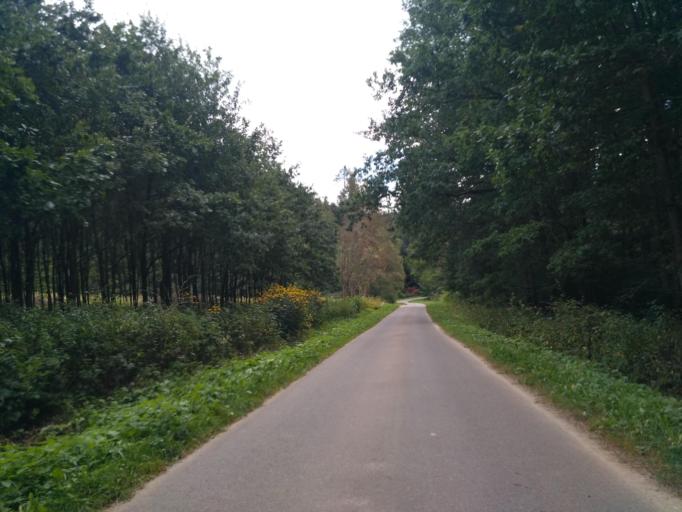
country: PL
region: Subcarpathian Voivodeship
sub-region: Powiat rzeszowski
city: Dynow
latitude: 49.7576
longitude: 22.2876
